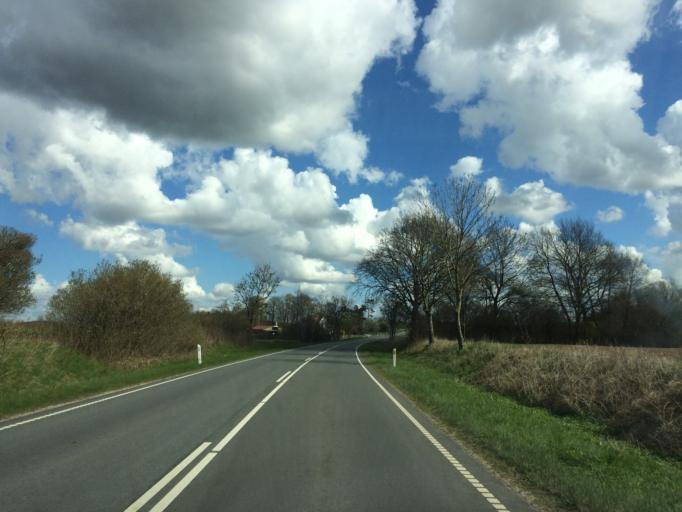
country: DK
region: South Denmark
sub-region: Assens Kommune
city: Harby
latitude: 55.2268
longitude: 10.1766
